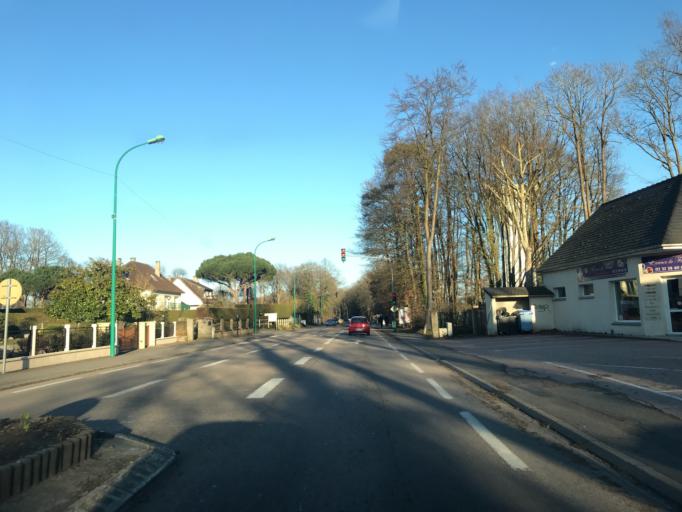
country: FR
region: Haute-Normandie
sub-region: Departement de l'Eure
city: Saint-Sebastien-de-Morsent
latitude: 49.0085
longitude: 1.0905
